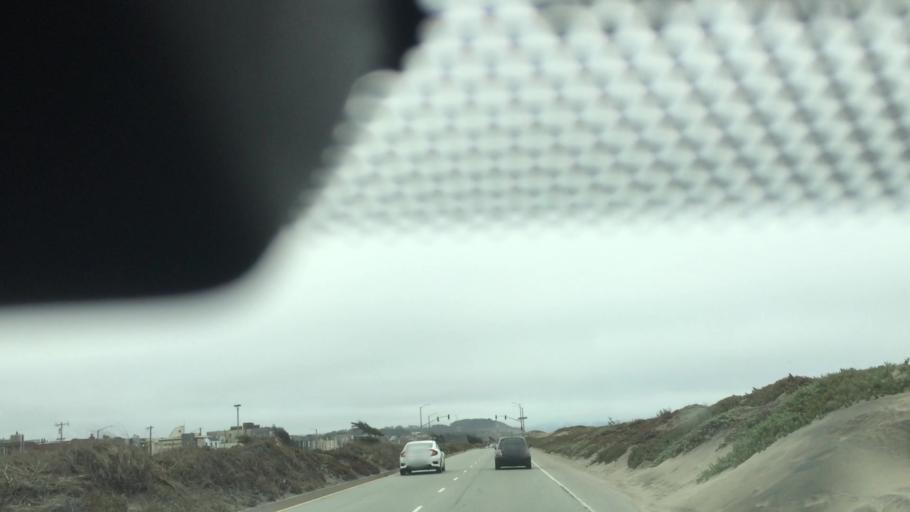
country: US
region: California
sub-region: San Mateo County
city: Daly City
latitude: 37.7432
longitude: -122.5079
